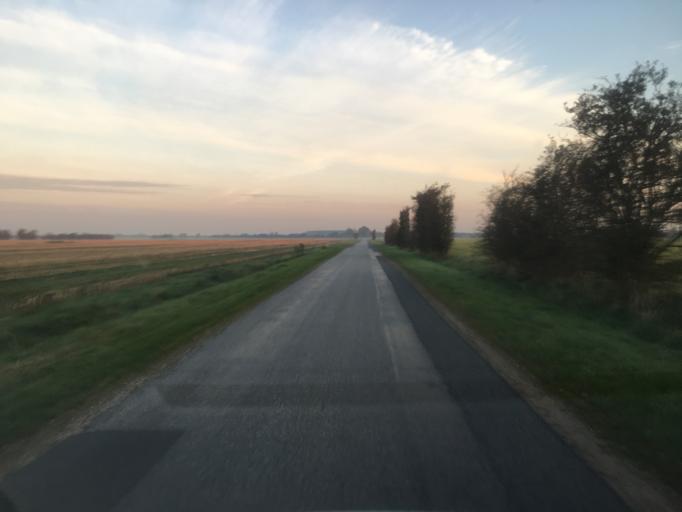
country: DK
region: South Denmark
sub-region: Tonder Kommune
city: Logumkloster
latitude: 55.0422
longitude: 9.0274
